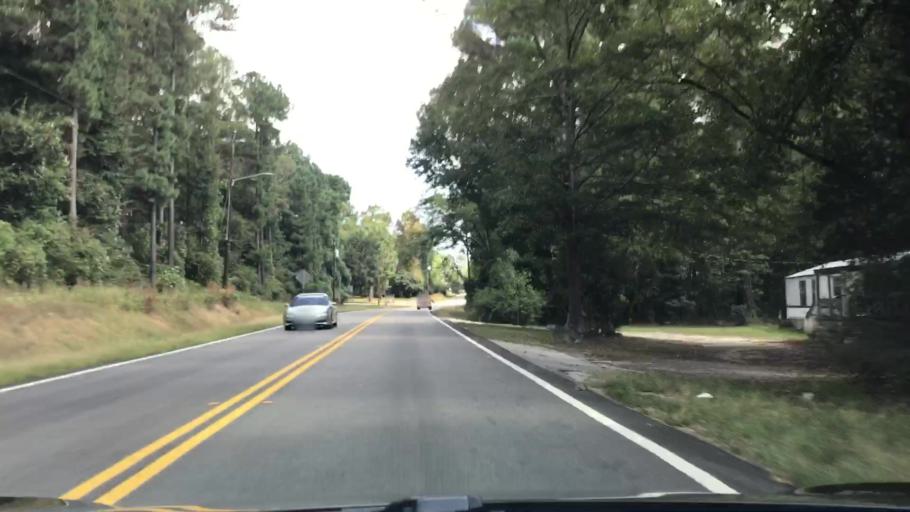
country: US
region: Georgia
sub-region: Greene County
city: Union Point
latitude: 33.5394
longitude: -83.0891
